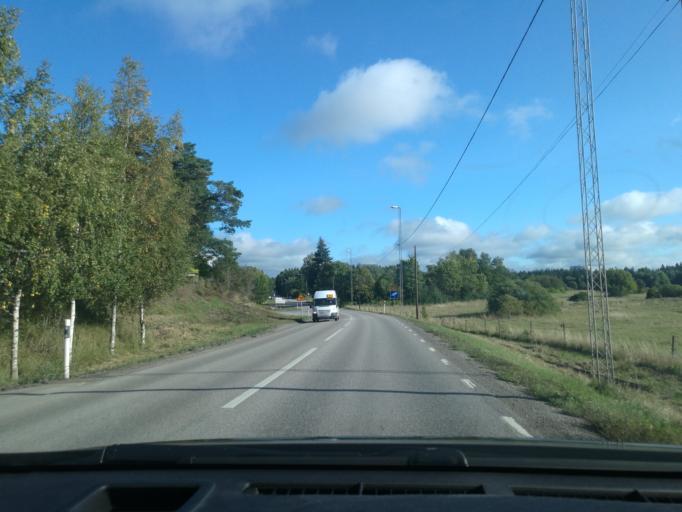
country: SE
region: Stockholm
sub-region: Upplands Vasby Kommun
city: Upplands Vaesby
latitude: 59.5251
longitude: 17.9637
